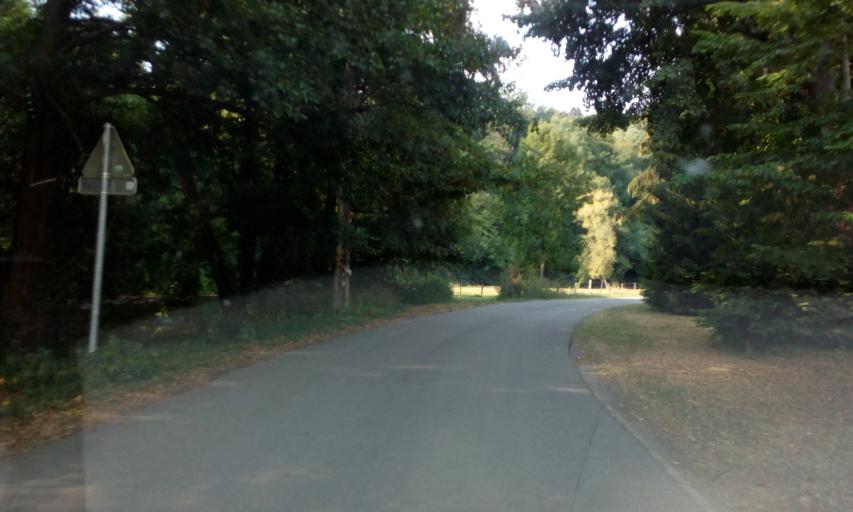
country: BE
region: Wallonia
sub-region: Province du Luxembourg
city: Tellin
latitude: 50.1084
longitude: 5.1971
